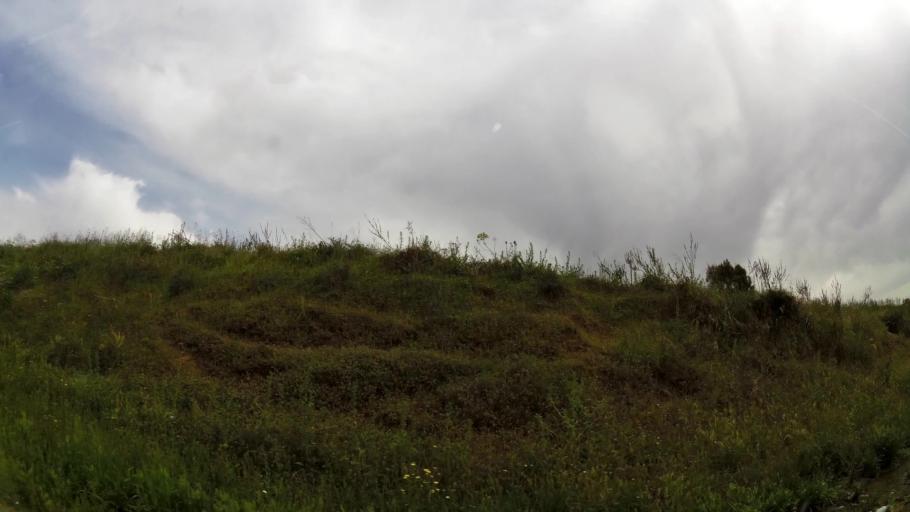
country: MA
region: Rabat-Sale-Zemmour-Zaer
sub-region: Khemisset
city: Khemisset
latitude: 33.7591
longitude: -6.2078
